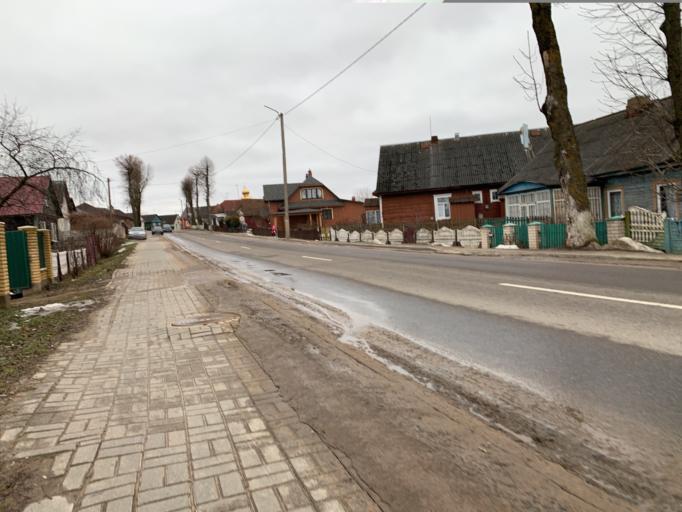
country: BY
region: Minsk
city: Nyasvizh
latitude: 53.2260
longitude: 26.6781
